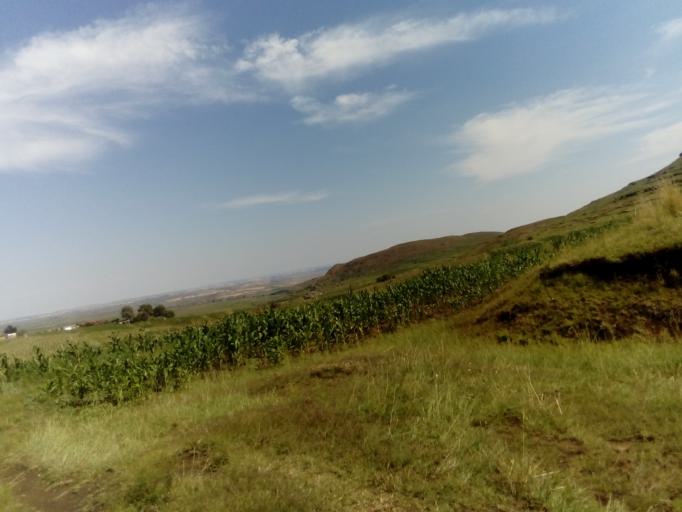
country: LS
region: Berea
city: Teyateyaneng
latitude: -29.2238
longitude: 27.8656
